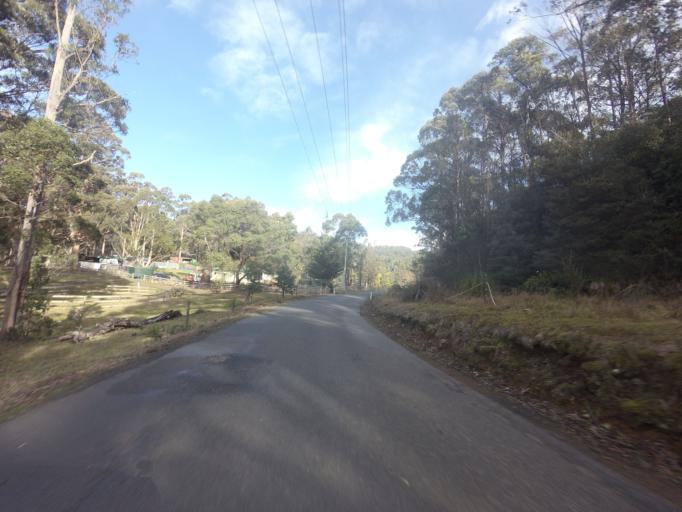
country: AU
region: Tasmania
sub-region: Kingborough
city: Margate
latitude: -43.0115
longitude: 147.1652
